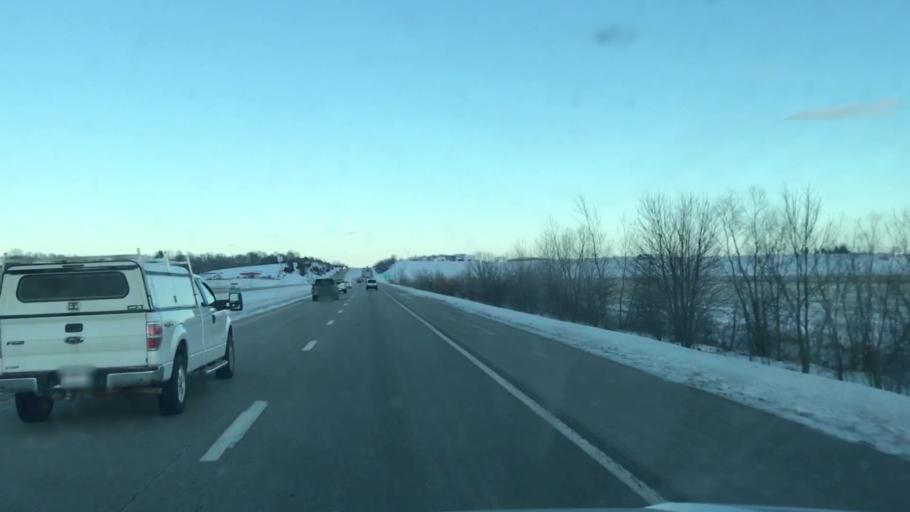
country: US
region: Missouri
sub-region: Buchanan County
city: Saint Joseph
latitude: 39.7477
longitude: -94.7202
